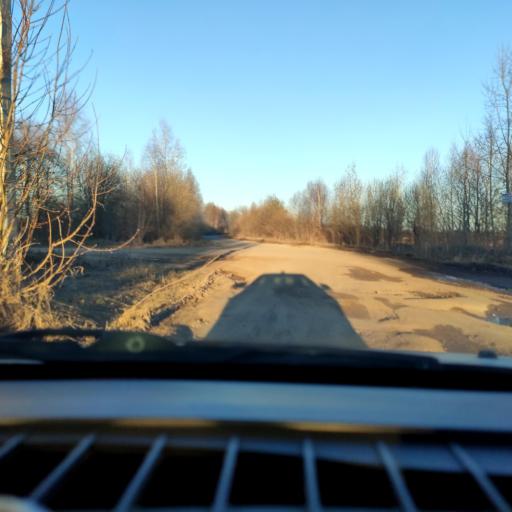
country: RU
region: Perm
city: Kultayevo
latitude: 57.9520
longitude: 55.9922
